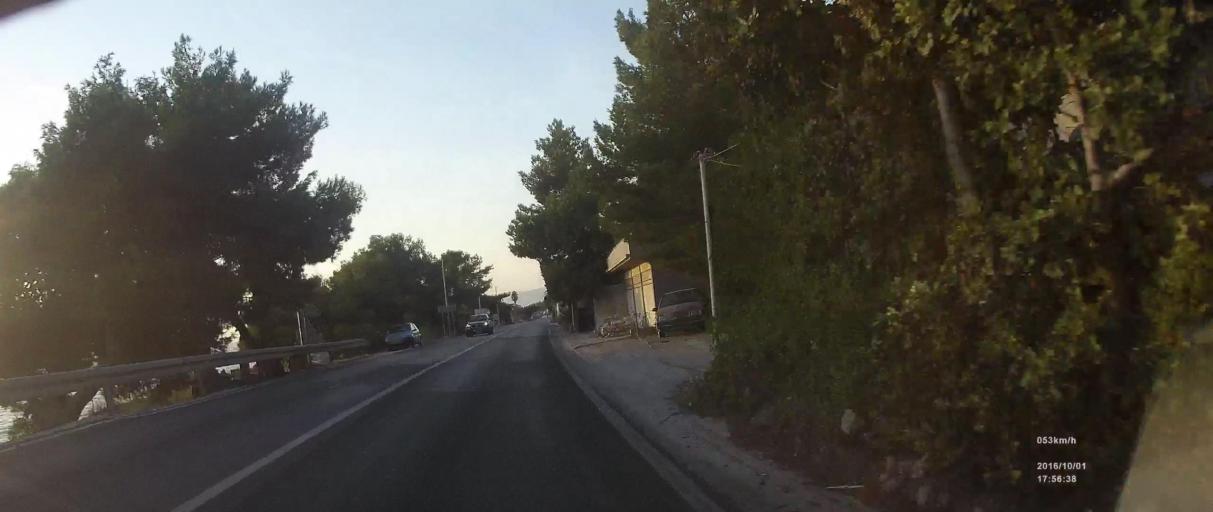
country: HR
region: Splitsko-Dalmatinska
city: Srinjine
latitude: 43.4650
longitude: 16.5807
